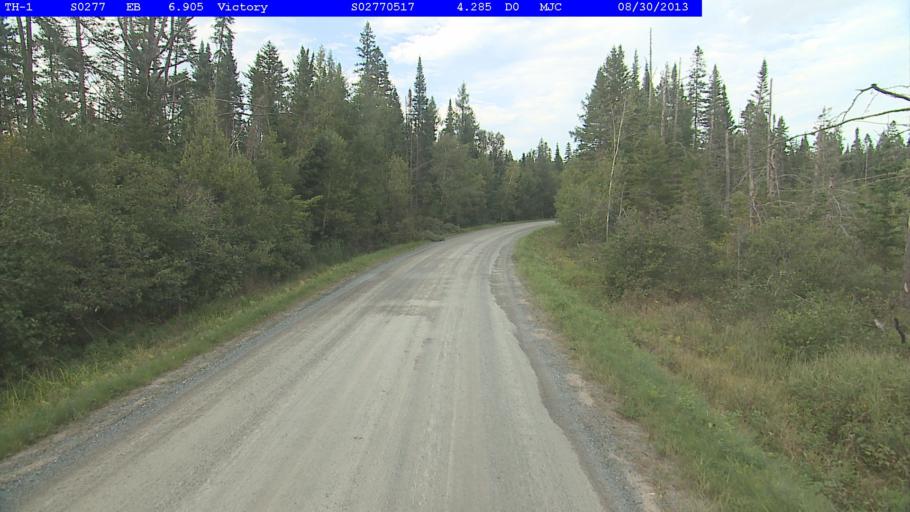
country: US
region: Vermont
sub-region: Caledonia County
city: Lyndonville
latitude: 44.5330
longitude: -71.7943
